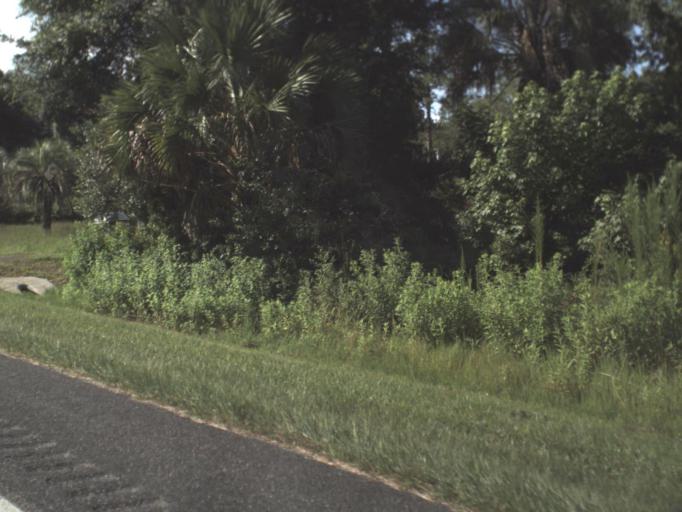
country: US
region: Florida
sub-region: Alachua County
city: Gainesville
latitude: 29.5442
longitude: -82.3197
